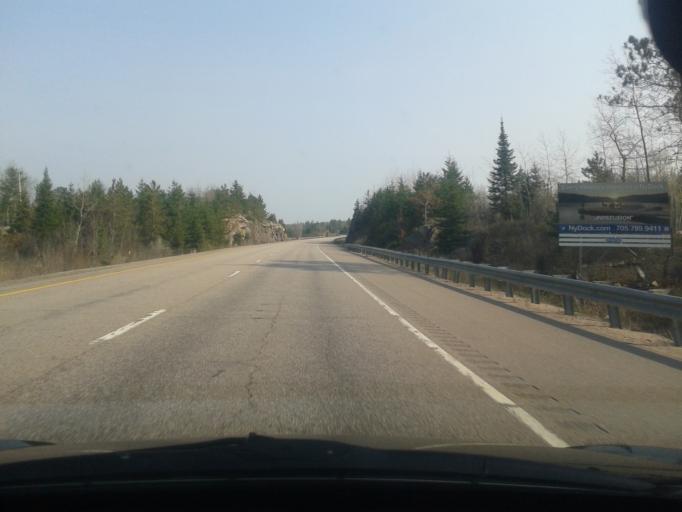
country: CA
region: Ontario
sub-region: Nipissing District
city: North Bay
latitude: 46.2255
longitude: -79.3497
